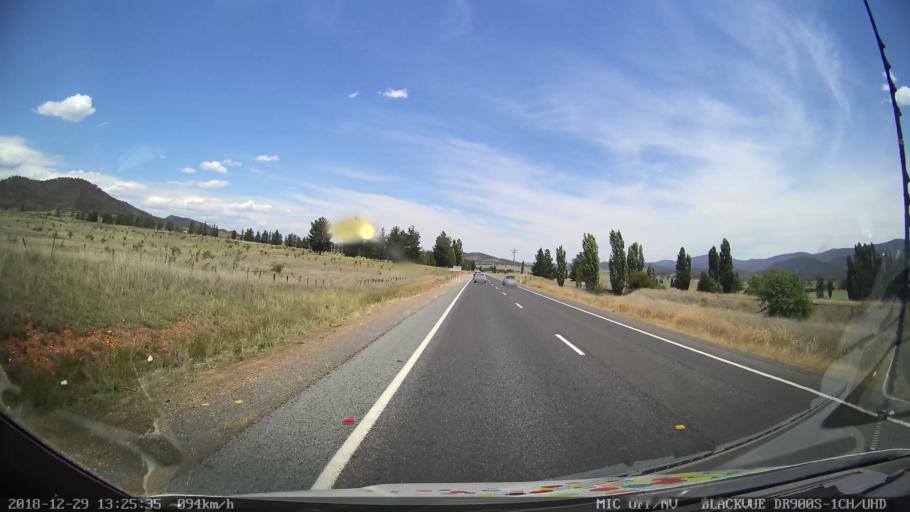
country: AU
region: New South Wales
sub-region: Cooma-Monaro
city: Cooma
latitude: -35.8445
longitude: 149.1612
